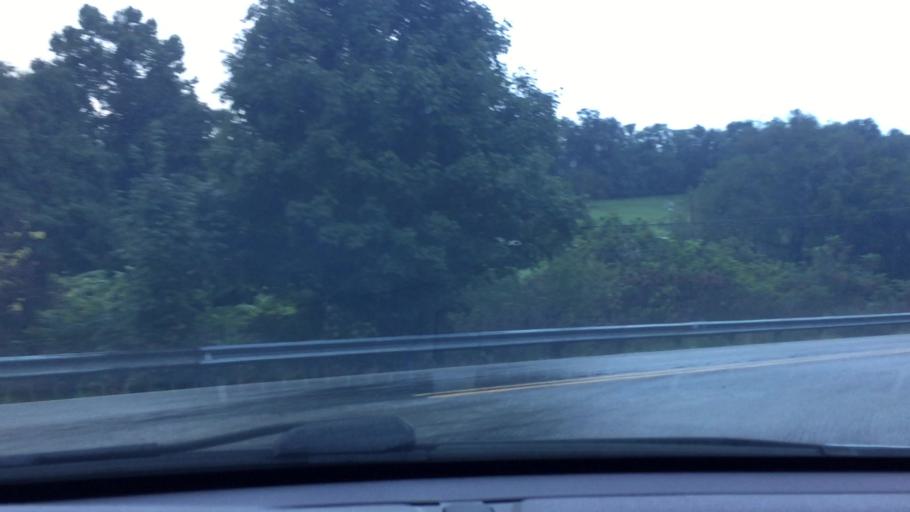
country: US
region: Pennsylvania
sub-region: Washington County
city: Charleroi
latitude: 40.1149
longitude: -79.9406
